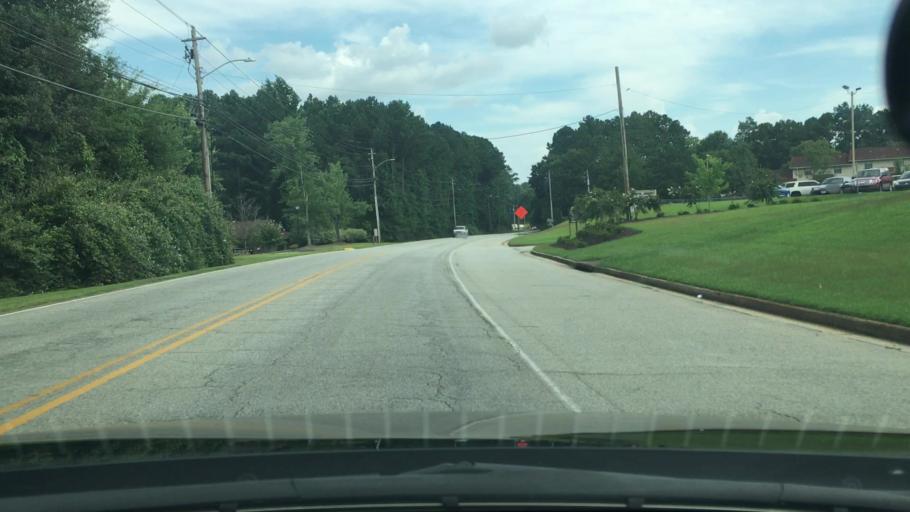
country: US
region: Georgia
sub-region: Coweta County
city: Newnan
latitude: 33.3825
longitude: -84.7826
